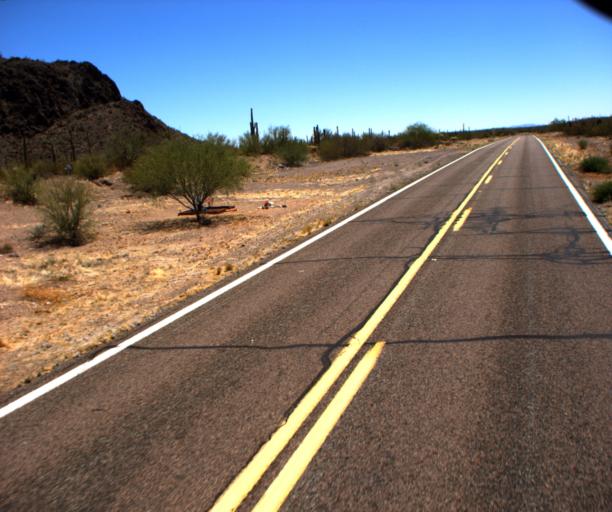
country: US
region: Arizona
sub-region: Pima County
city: Ajo
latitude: 32.2225
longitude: -112.6956
